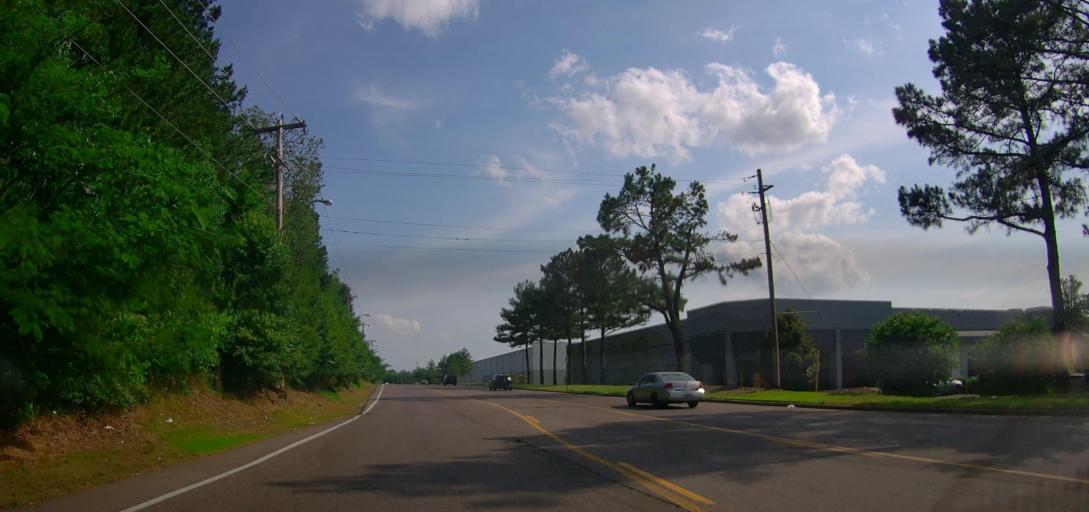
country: US
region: Mississippi
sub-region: De Soto County
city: Olive Branch
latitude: 35.0184
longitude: -89.8487
